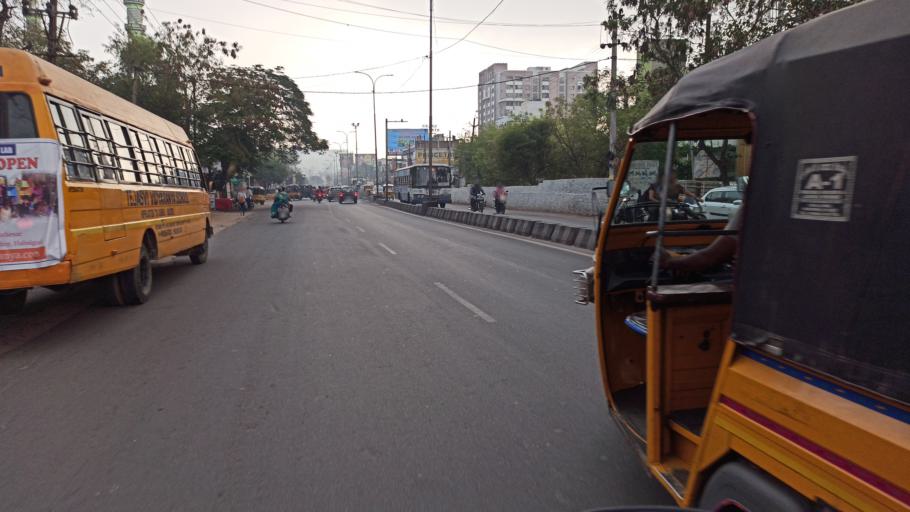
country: IN
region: Telangana
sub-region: Rangareddi
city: Uppal Kalan
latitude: 17.3988
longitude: 78.5350
